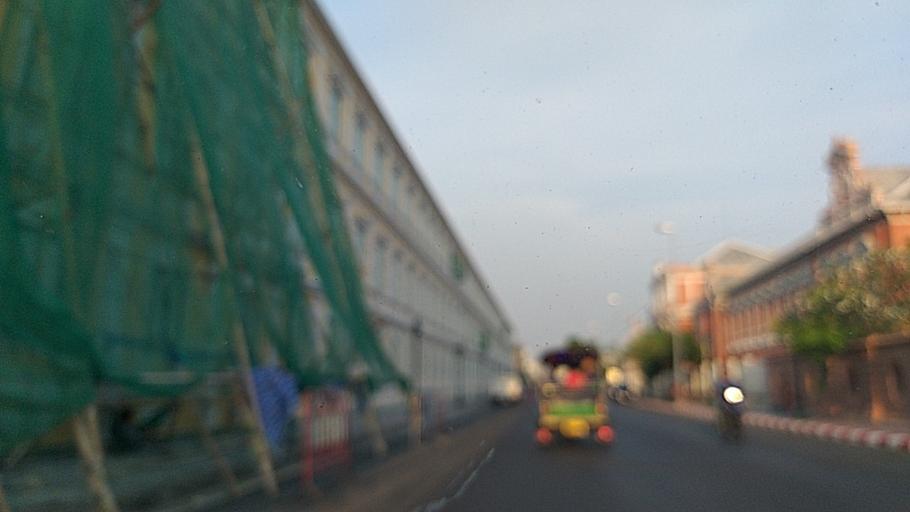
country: TH
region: Bangkok
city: Bangkok
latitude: 13.7511
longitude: 100.4945
